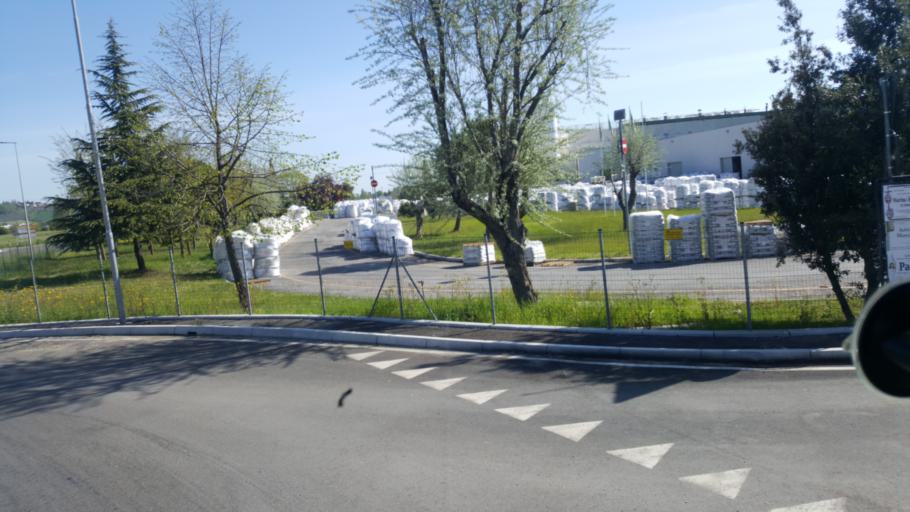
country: IT
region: Emilia-Romagna
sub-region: Provincia di Rimini
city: Poggio Berni
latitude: 44.0042
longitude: 12.4016
